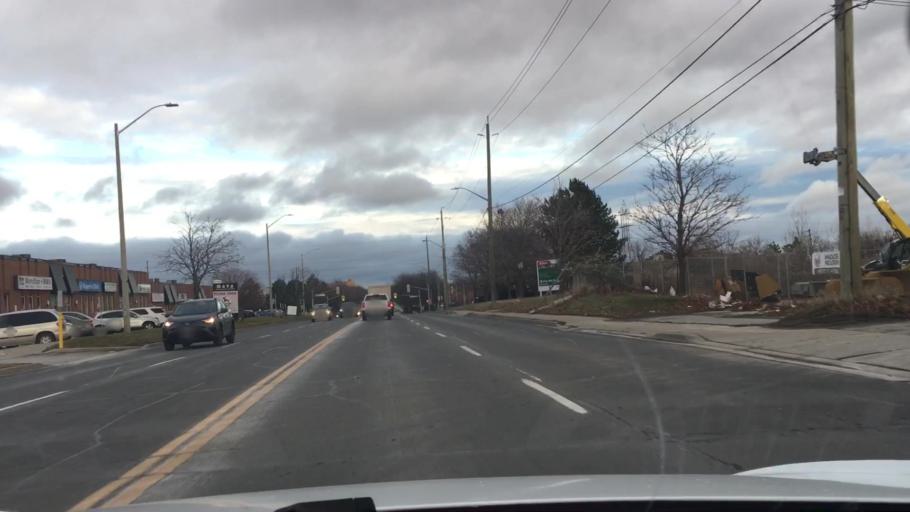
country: CA
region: Ontario
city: Willowdale
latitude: 43.8244
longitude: -79.3398
